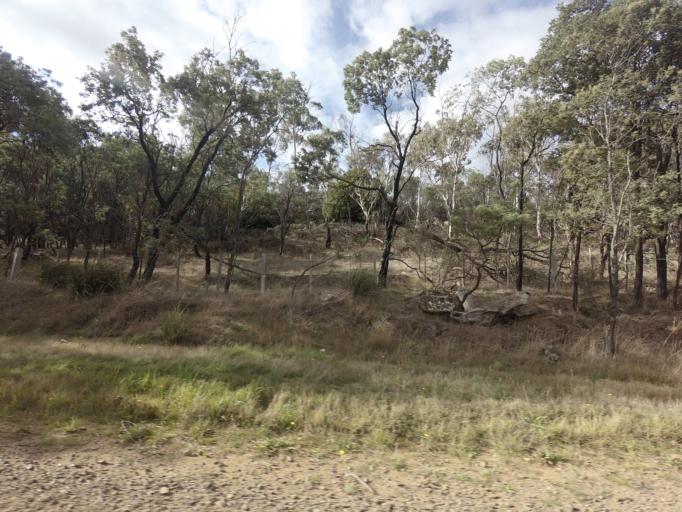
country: AU
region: Tasmania
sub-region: Brighton
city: Bridgewater
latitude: -42.4730
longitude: 147.2895
